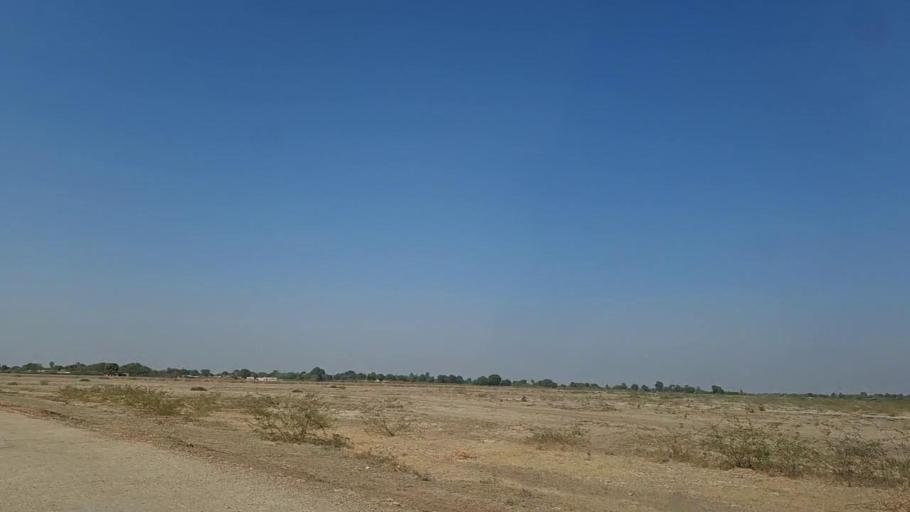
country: PK
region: Sindh
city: Samaro
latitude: 25.3962
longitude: 69.4017
